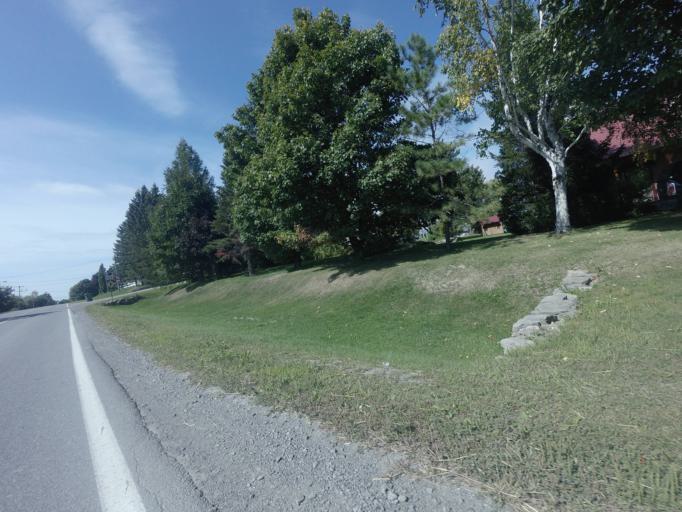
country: CA
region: Quebec
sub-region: Laurentides
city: Saint-Eustache
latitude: 45.5950
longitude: -73.9136
